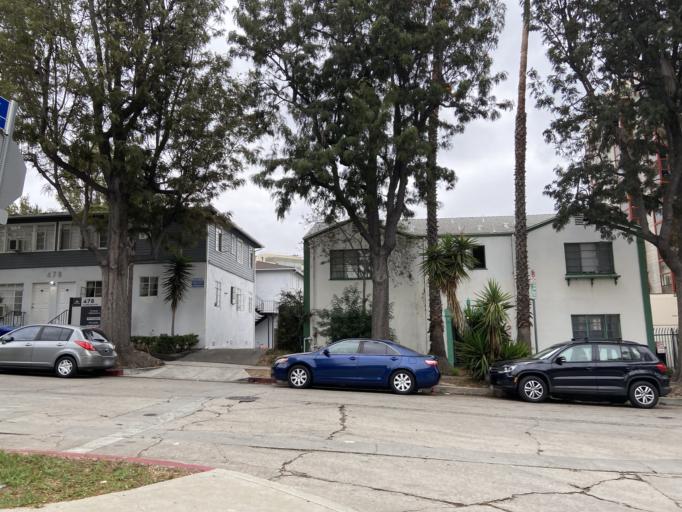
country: US
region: California
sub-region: Los Angeles County
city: Westwood, Los Angeles
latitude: 34.0686
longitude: -118.4513
